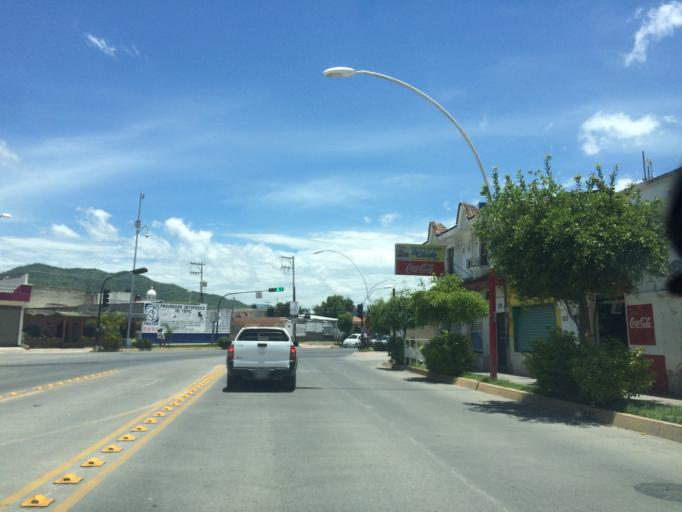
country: MX
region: Nayarit
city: Tepic
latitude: 21.4880
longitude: -104.8720
